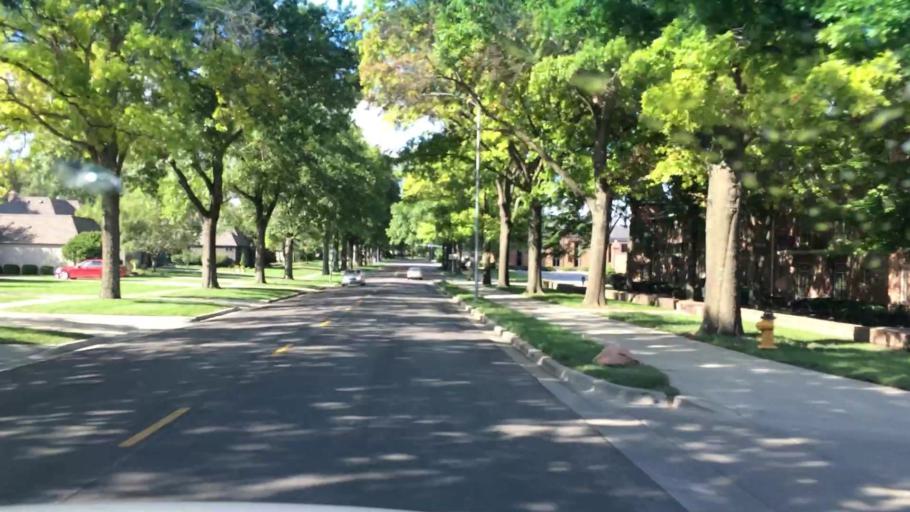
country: US
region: Kansas
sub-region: Johnson County
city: Prairie Village
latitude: 38.9764
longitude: -94.6343
